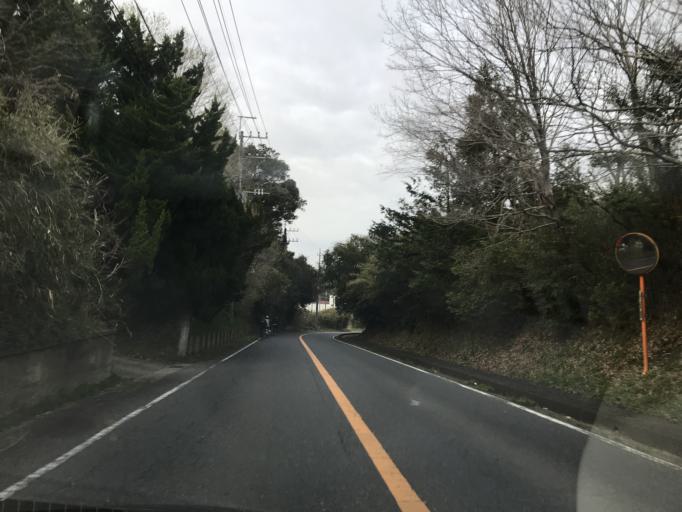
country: JP
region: Chiba
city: Omigawa
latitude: 35.8218
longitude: 140.5776
